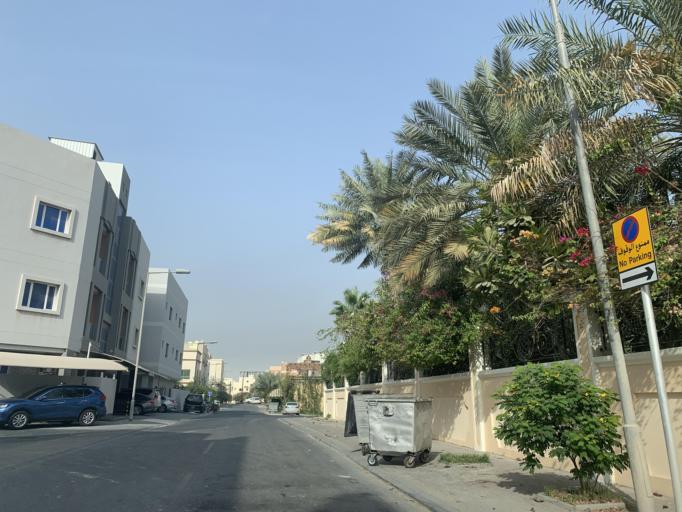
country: BH
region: Northern
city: Madinat `Isa
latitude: 26.1896
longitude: 50.5629
